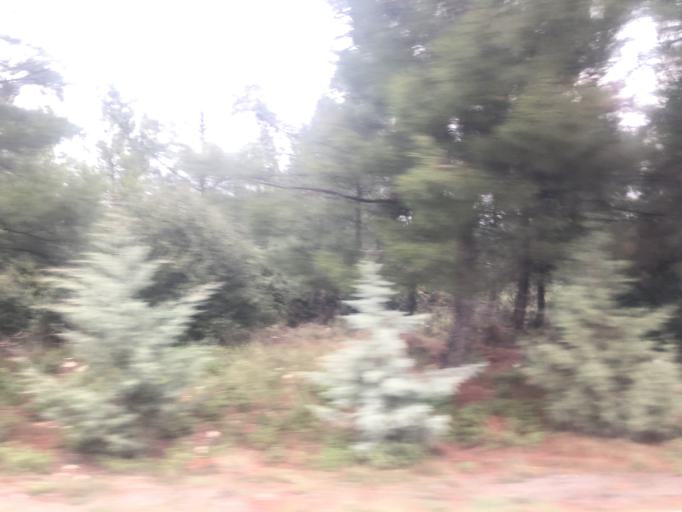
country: TR
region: Izmir
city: Buca
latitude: 38.3682
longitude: 27.2173
